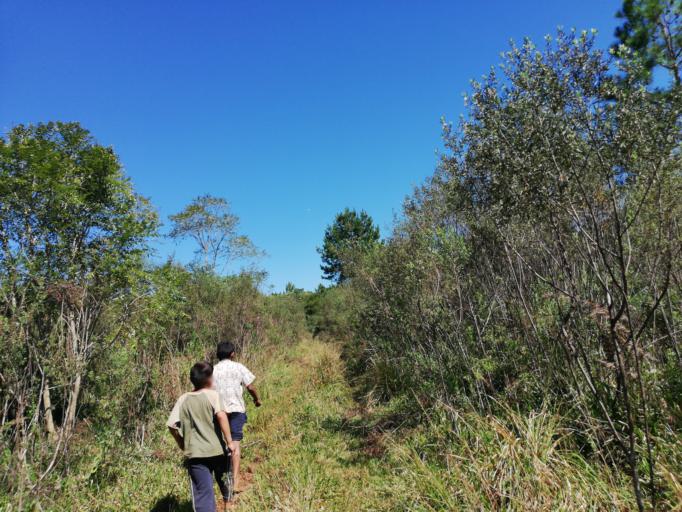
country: AR
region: Misiones
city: El Soberbio
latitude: -27.0624
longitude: -54.3766
